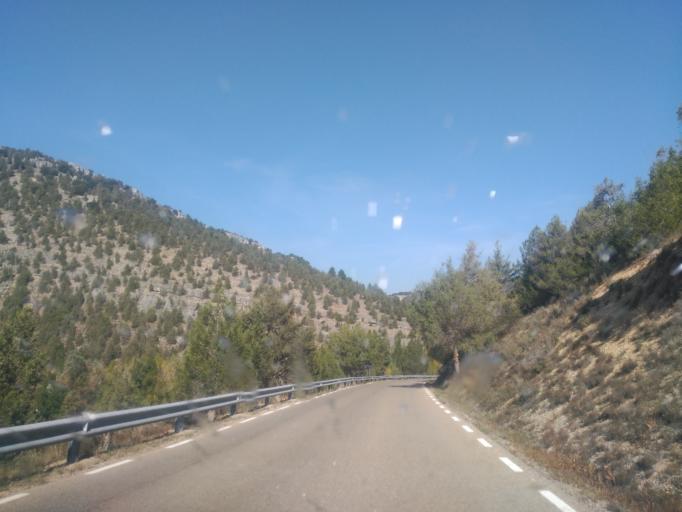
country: ES
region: Castille and Leon
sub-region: Provincia de Soria
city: Ucero
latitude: 41.7288
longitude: -3.0449
